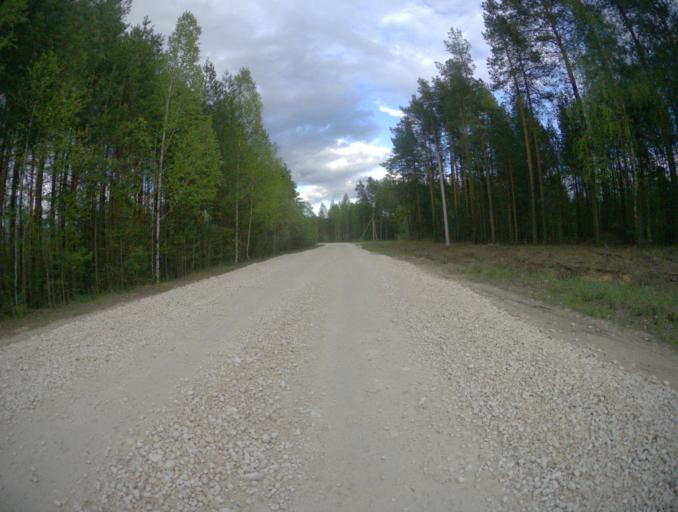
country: RU
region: Vladimir
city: Anopino
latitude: 55.7192
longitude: 40.6039
